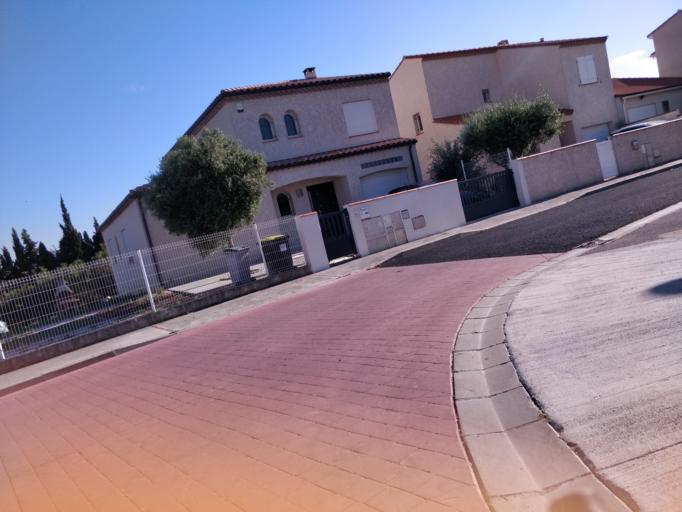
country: FR
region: Languedoc-Roussillon
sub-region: Departement des Pyrenees-Orientales
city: Saleilles
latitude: 42.6573
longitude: 2.9402
